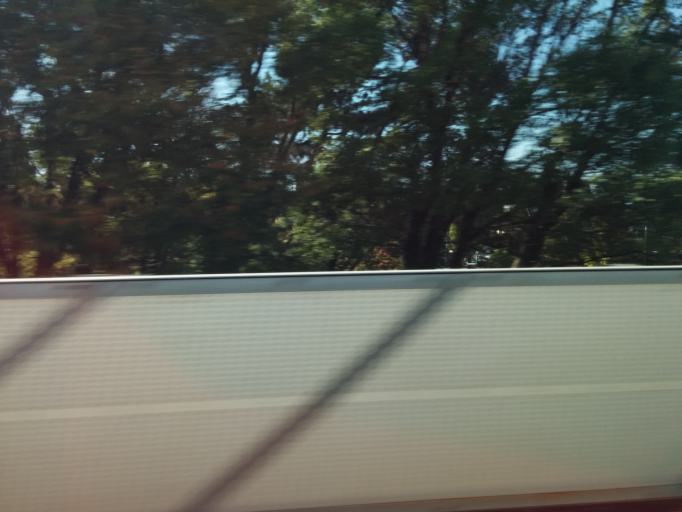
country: JP
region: Aichi
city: Inazawa
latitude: 35.2172
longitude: 136.8413
